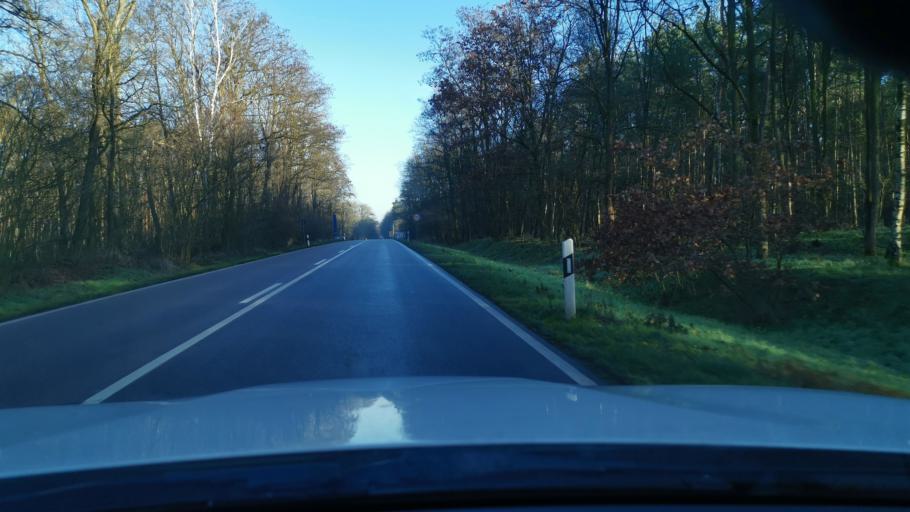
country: DE
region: Saxony-Anhalt
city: Abtsdorf
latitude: 51.9295
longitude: 12.7078
